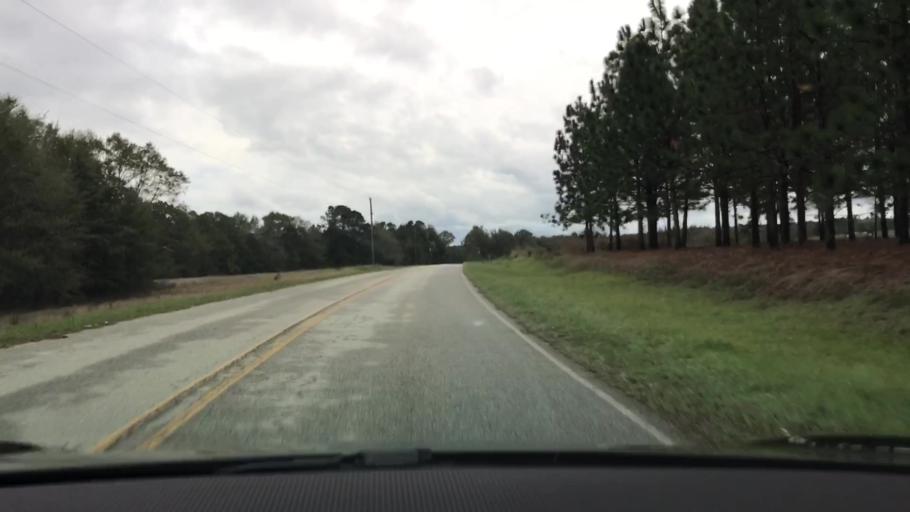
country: US
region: Georgia
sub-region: Jefferson County
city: Wadley
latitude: 32.8422
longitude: -82.3949
